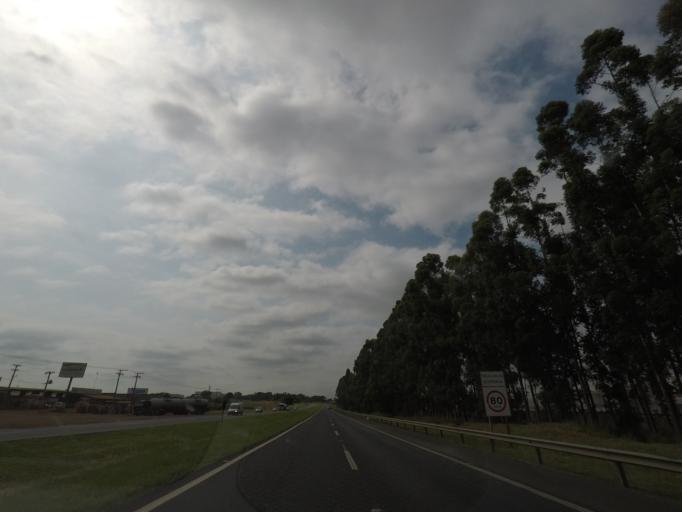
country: BR
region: Sao Paulo
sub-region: Paulinia
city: Paulinia
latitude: -22.7701
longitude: -47.1373
